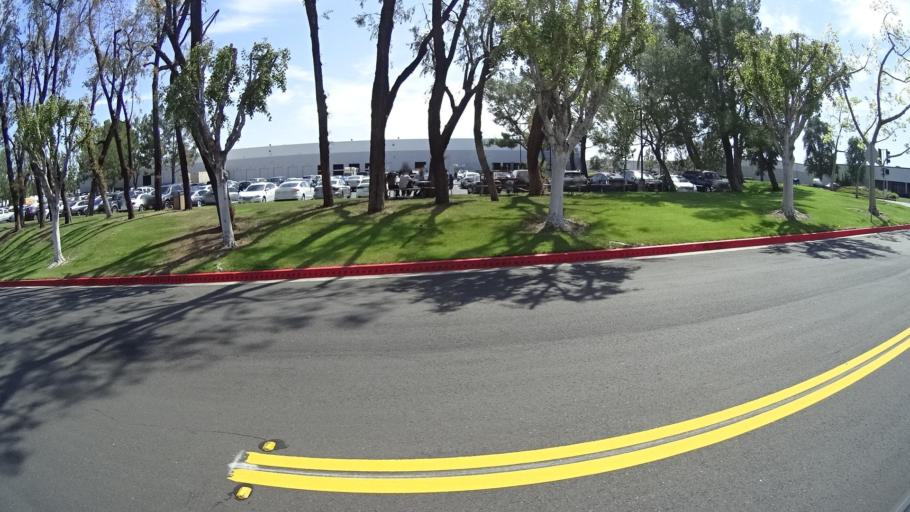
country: US
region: California
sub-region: Los Angeles County
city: South San Jose Hills
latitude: 34.0016
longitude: -117.9110
